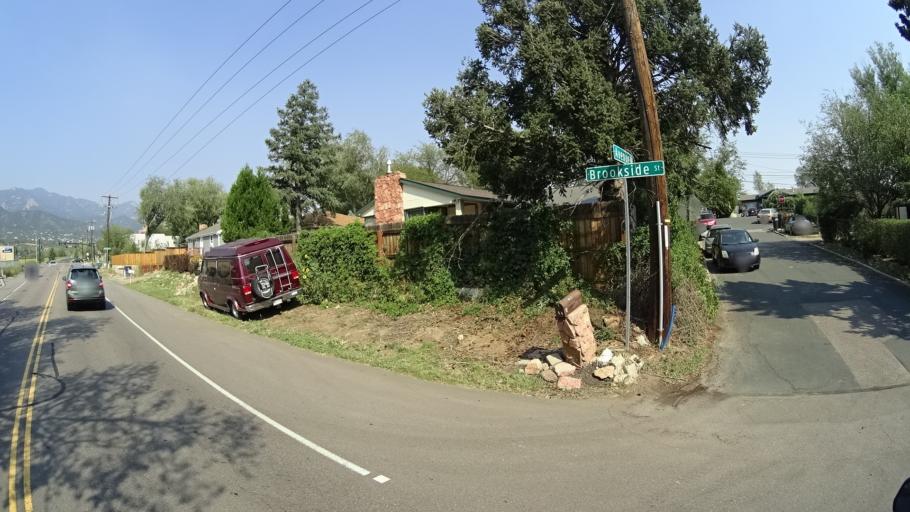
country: US
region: Colorado
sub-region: El Paso County
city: Colorado Springs
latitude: 38.8129
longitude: -104.8389
